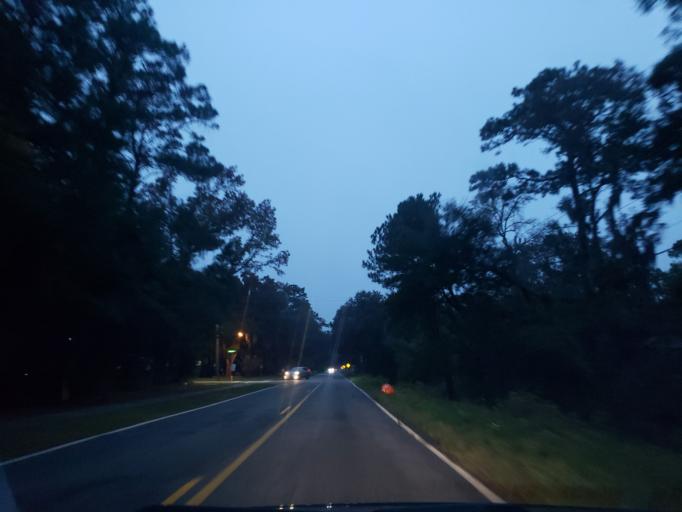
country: US
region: Georgia
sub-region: Chatham County
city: Wilmington Island
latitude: 32.0213
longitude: -80.9643
